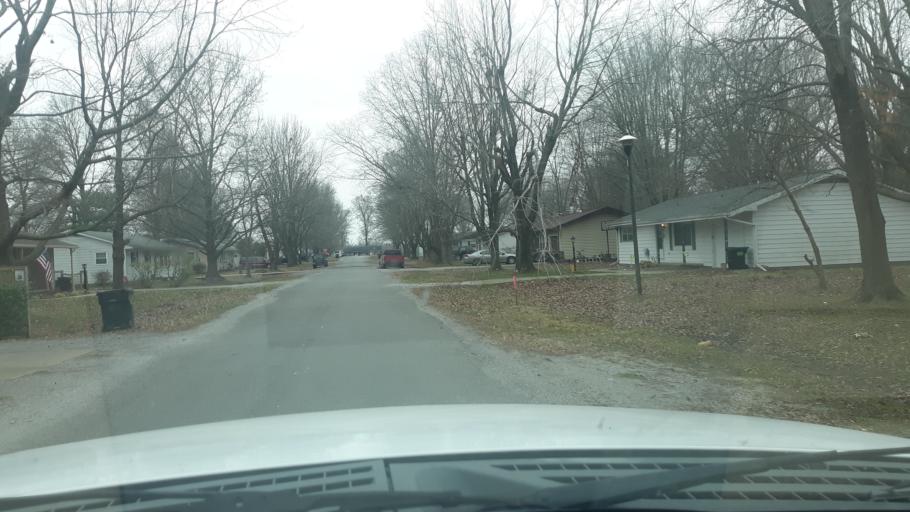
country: US
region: Illinois
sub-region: Saline County
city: Harrisburg
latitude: 37.8368
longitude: -88.6083
